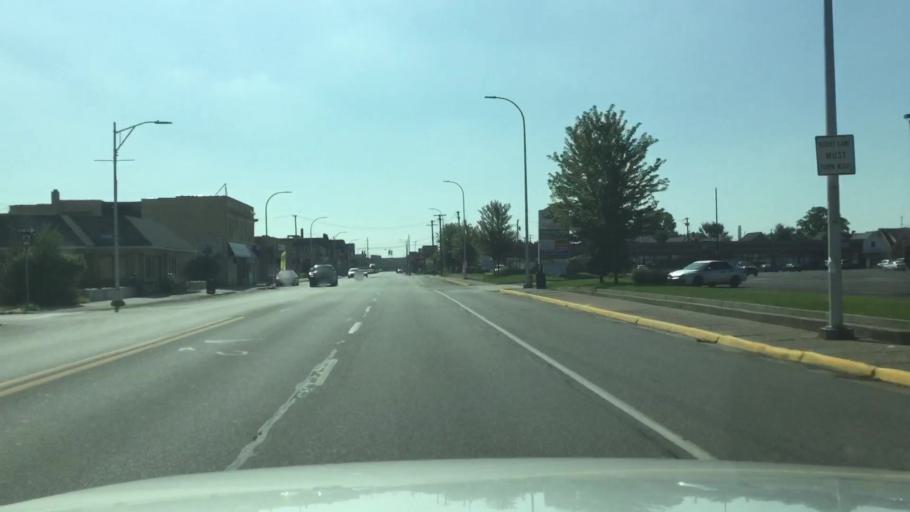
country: US
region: Michigan
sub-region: Wayne County
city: Hamtramck
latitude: 42.3933
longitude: -83.0556
